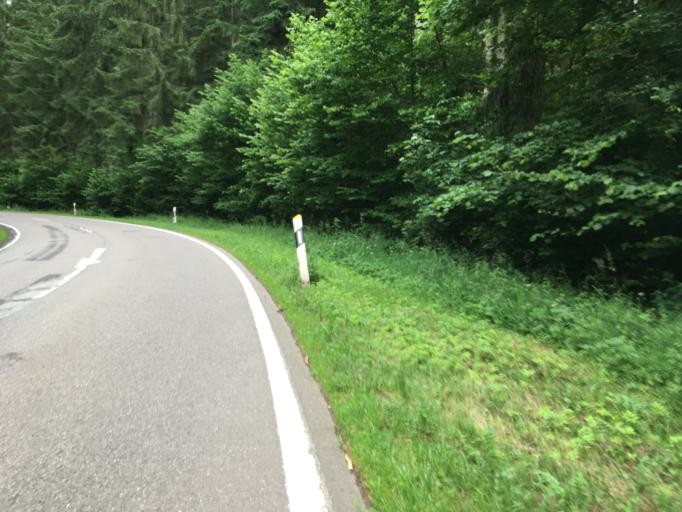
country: DE
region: Saarland
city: Saarhoelzbach
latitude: 49.4976
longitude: 6.6394
